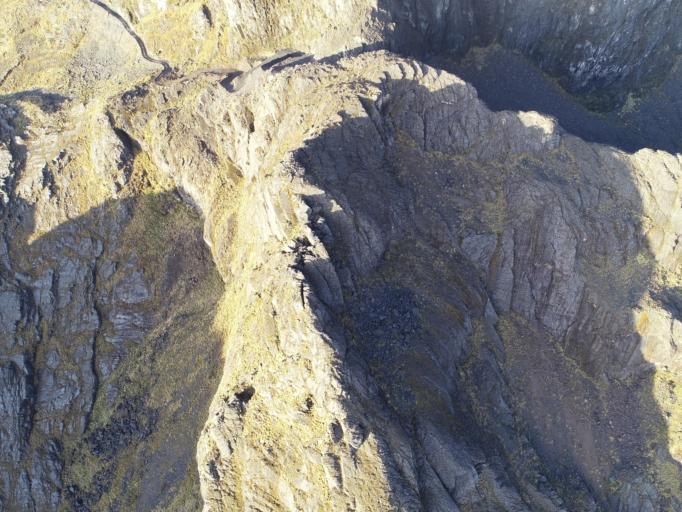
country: PE
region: Puno
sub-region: San Antonio De Putina
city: Sina
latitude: -14.7348
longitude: -69.0489
